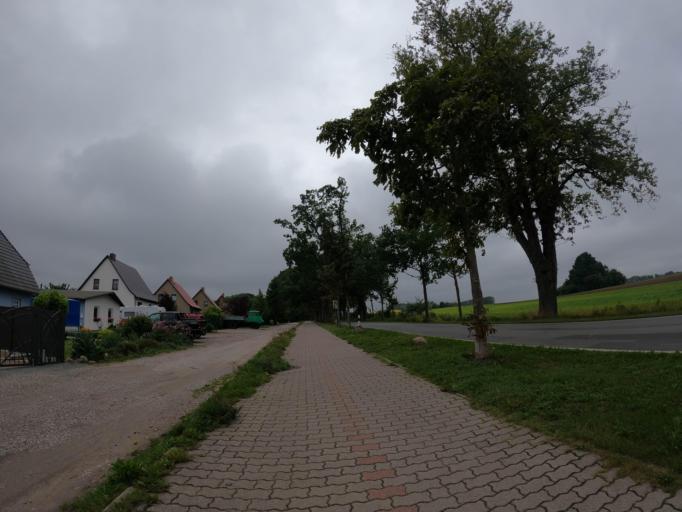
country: DE
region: Mecklenburg-Vorpommern
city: Putbus
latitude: 54.3471
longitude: 13.4951
